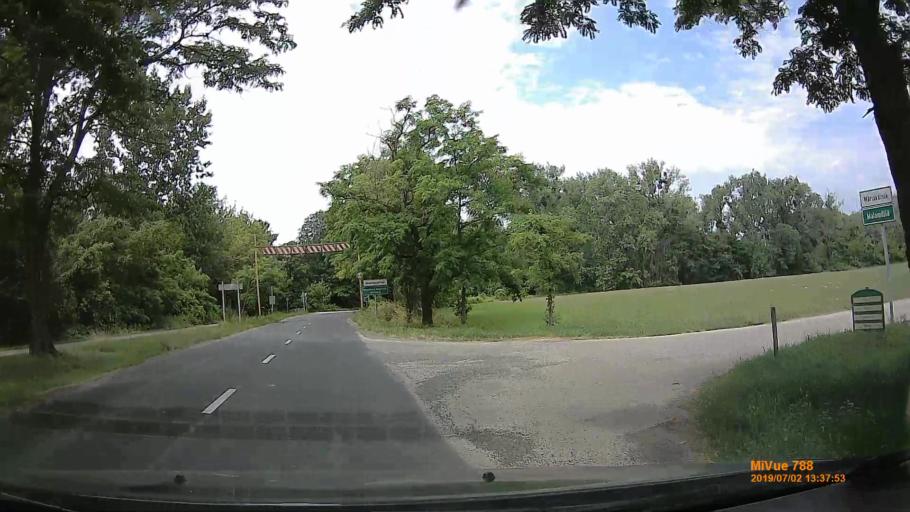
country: HU
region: Gyor-Moson-Sopron
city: Mosonmagyarovar
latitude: 47.8565
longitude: 17.2925
